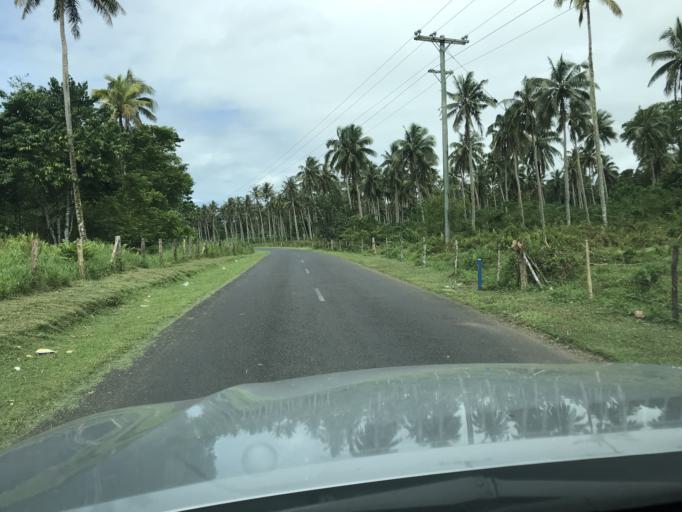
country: WS
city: Fasito`outa
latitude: -13.8728
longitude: -171.9173
